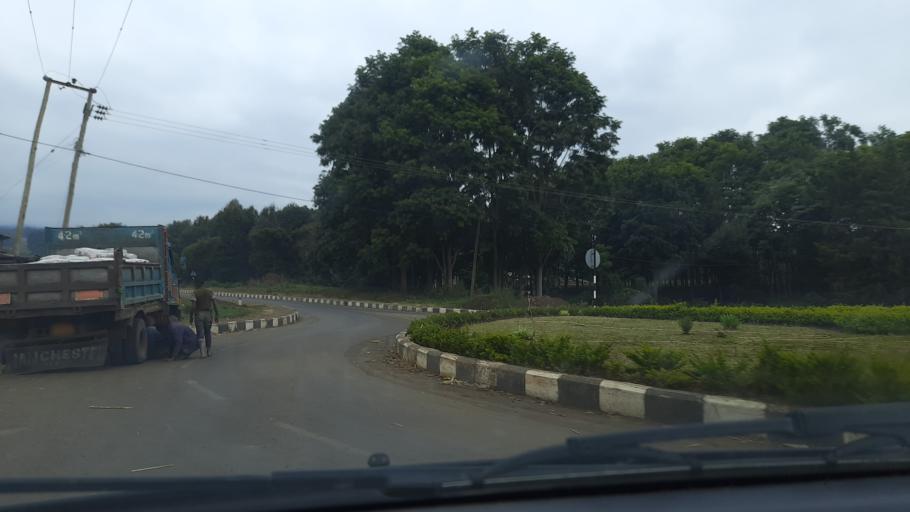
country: TZ
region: Kilimanjaro
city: Moshi
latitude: -2.9342
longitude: 37.4685
